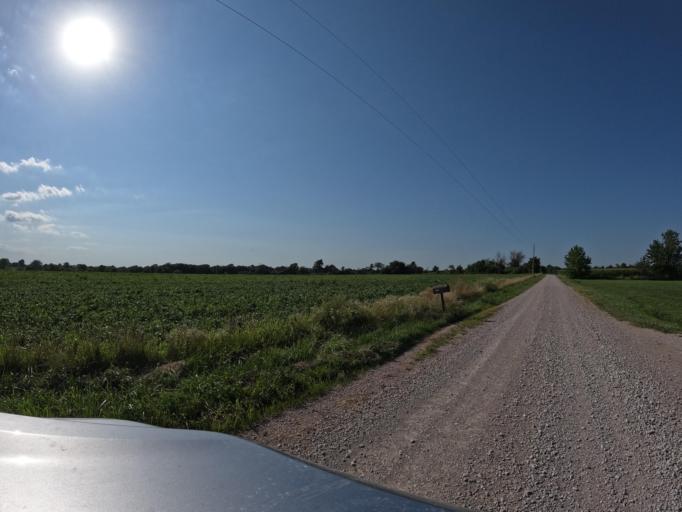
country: US
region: Iowa
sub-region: Appanoose County
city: Centerville
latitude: 40.7232
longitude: -93.0158
